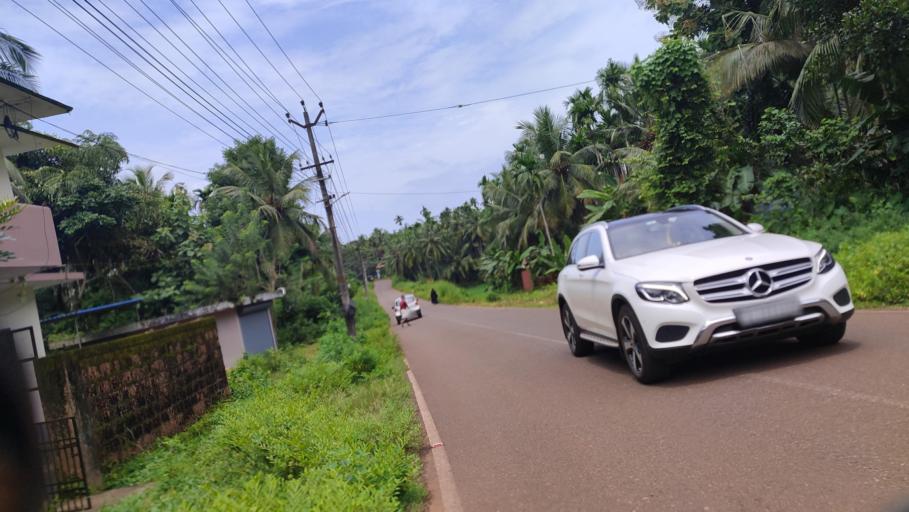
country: IN
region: Kerala
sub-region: Kasaragod District
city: Kannangad
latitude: 12.3968
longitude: 75.0554
